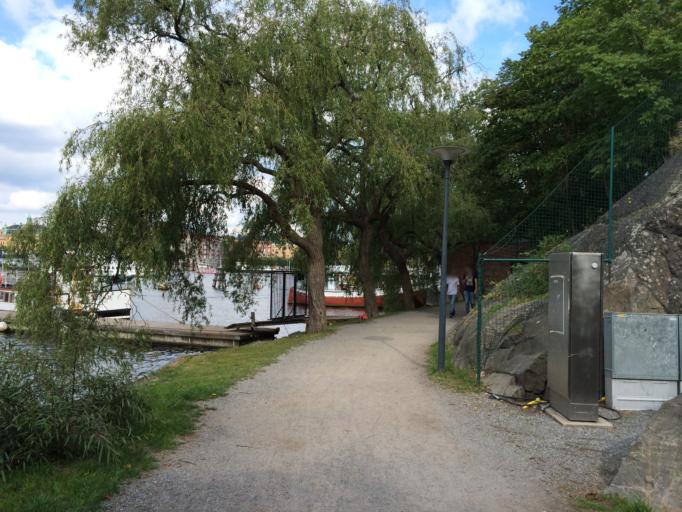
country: SE
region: Stockholm
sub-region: Stockholms Kommun
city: OEstermalm
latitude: 59.3273
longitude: 18.0809
